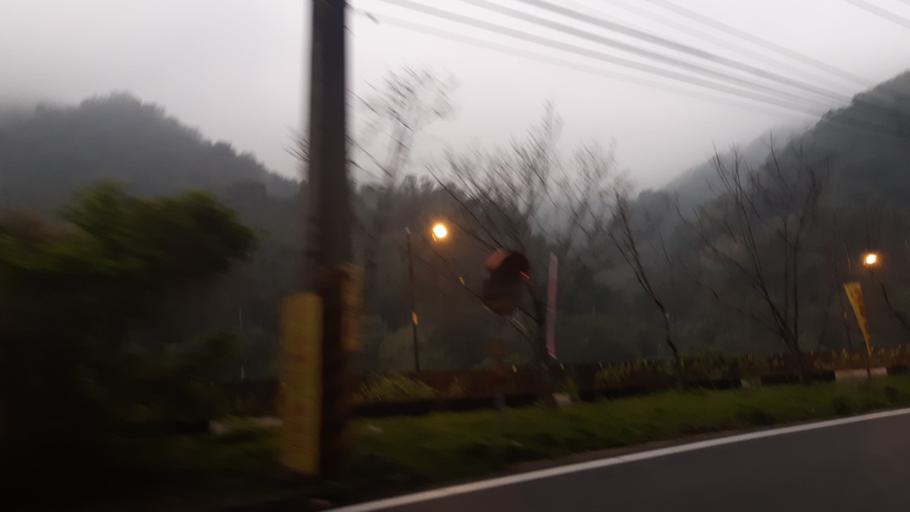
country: TW
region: Taiwan
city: Daxi
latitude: 24.6987
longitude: 121.1953
